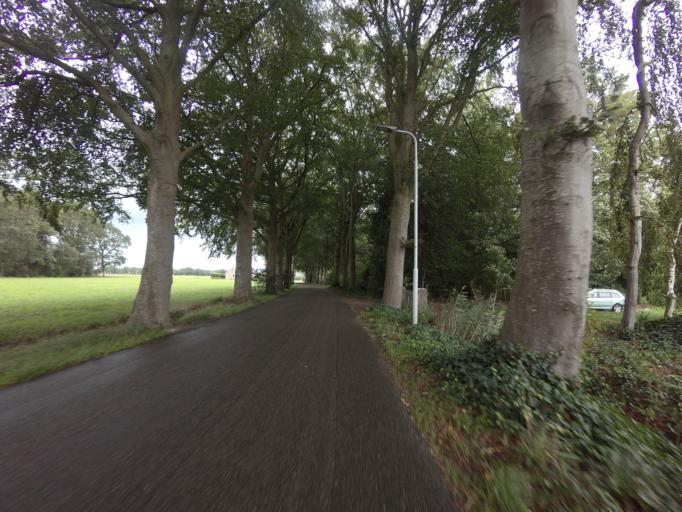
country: NL
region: Drenthe
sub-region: Gemeente Westerveld
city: Dwingeloo
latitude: 52.9698
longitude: 6.2927
